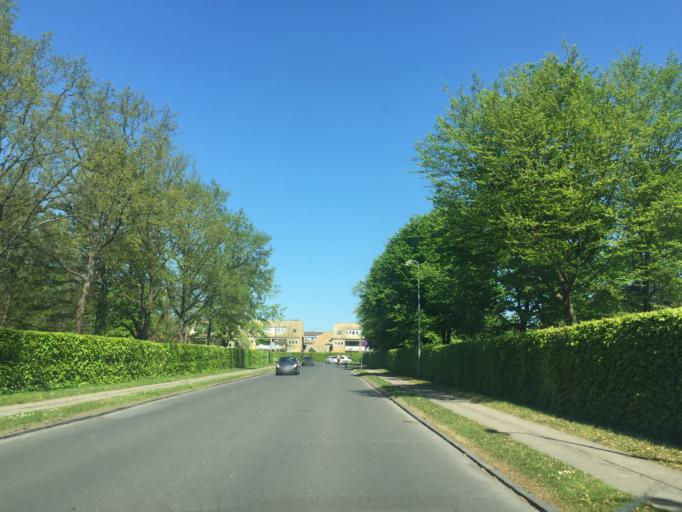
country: DK
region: South Denmark
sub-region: Odense Kommune
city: Odense
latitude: 55.3896
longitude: 10.3686
